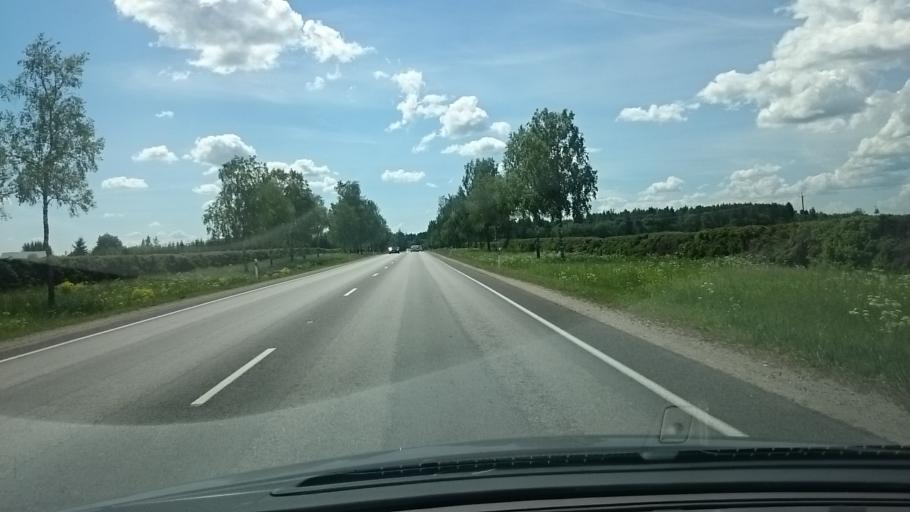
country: EE
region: Jaervamaa
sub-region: Paide linn
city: Paide
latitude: 58.9959
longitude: 25.5935
